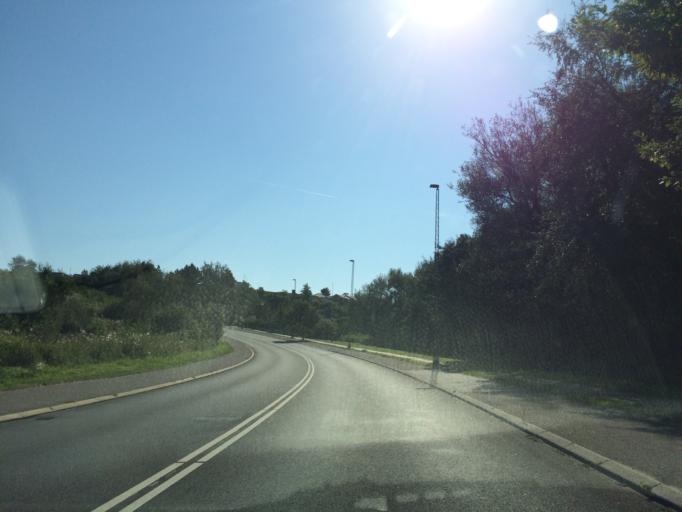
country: DK
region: South Denmark
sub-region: Kolding Kommune
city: Kolding
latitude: 55.5020
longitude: 9.5160
